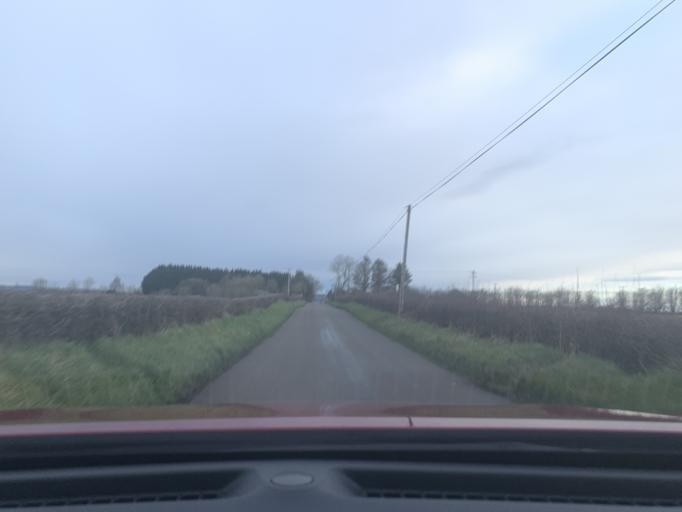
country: IE
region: Connaught
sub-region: Roscommon
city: Ballaghaderreen
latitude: 53.8787
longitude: -8.5627
